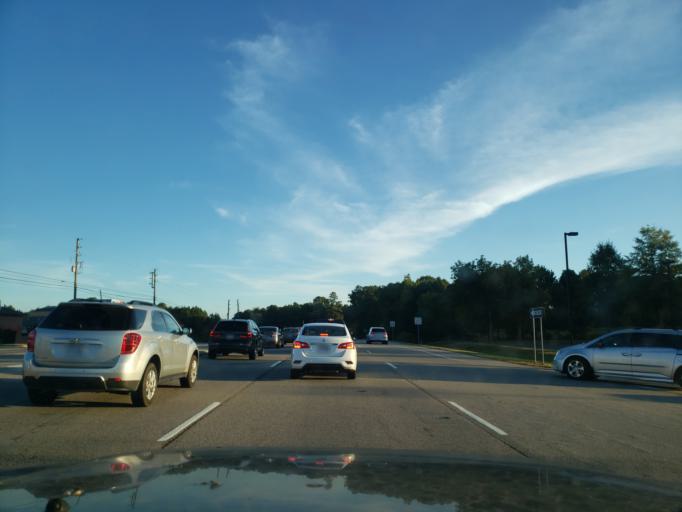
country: US
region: North Carolina
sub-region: Wake County
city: Morrisville
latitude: 35.8309
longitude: -78.8534
